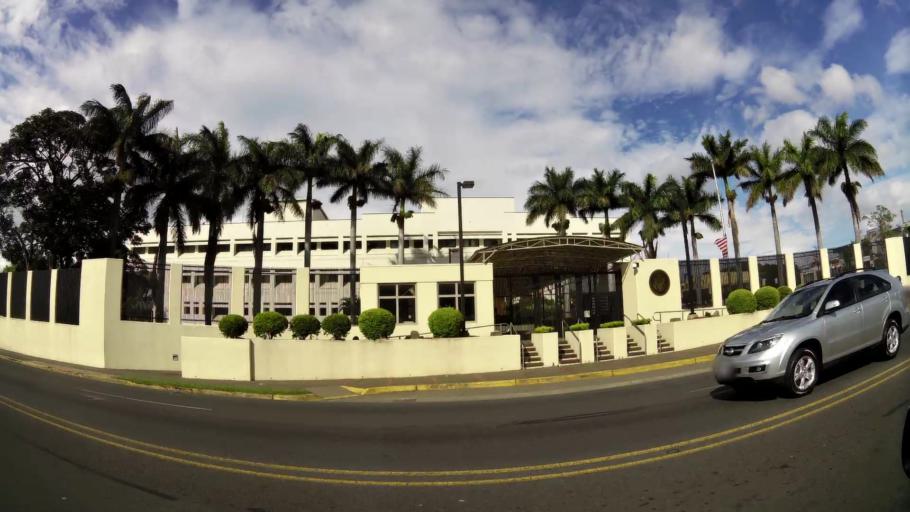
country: CR
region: San Jose
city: San Rafael
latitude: 9.9421
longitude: -84.1242
